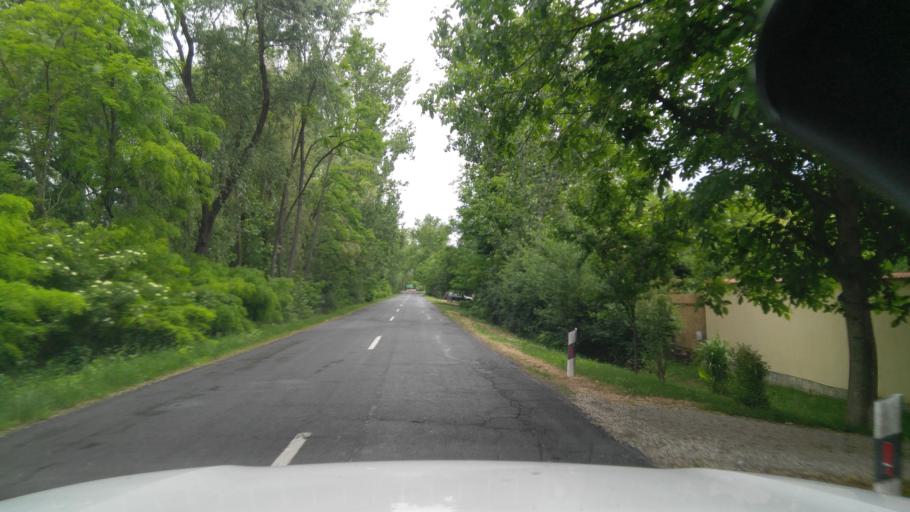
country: HU
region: Bekes
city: Bekes
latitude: 46.7047
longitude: 21.1718
